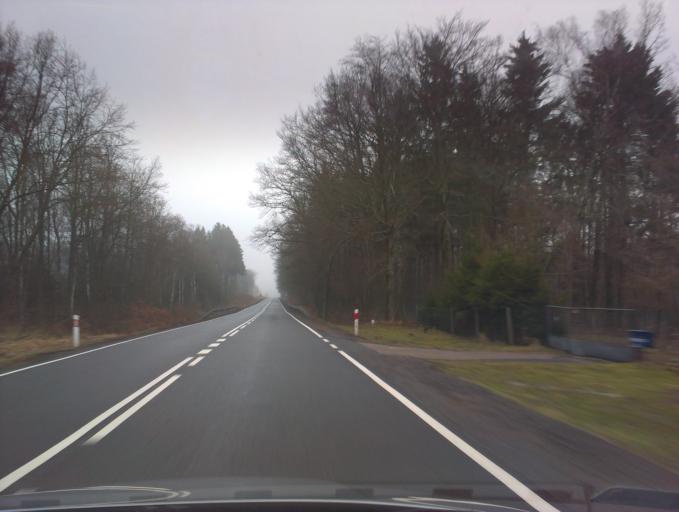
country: PL
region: West Pomeranian Voivodeship
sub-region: Powiat koszalinski
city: Bobolice
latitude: 53.8860
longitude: 16.6134
